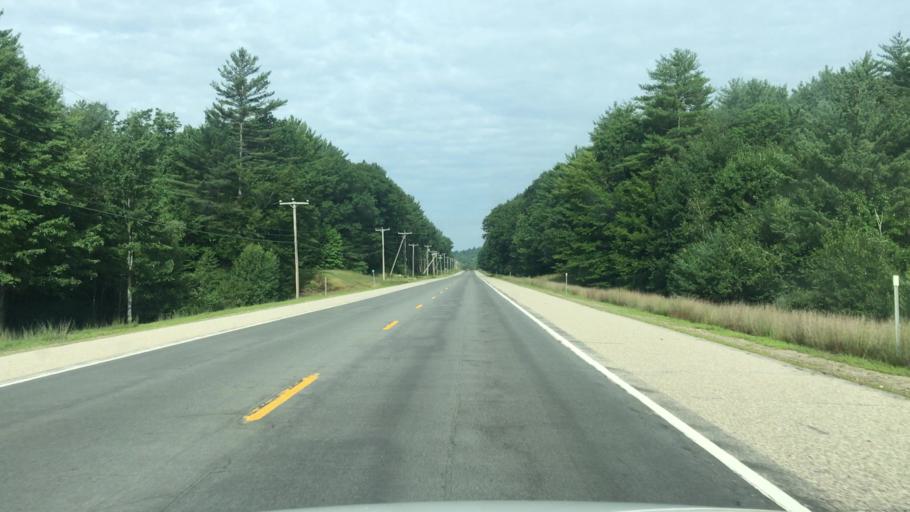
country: US
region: New Hampshire
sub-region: Carroll County
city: Tamworth
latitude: 43.8269
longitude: -71.2548
